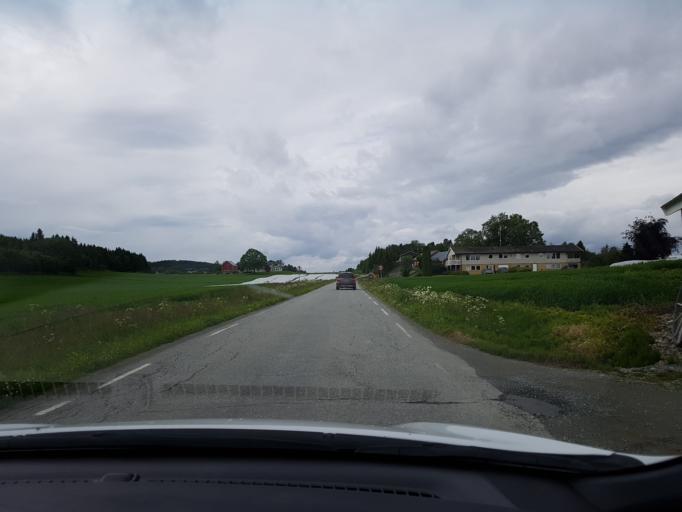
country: NO
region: Nord-Trondelag
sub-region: Frosta
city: Frosta
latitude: 63.6302
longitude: 10.7746
